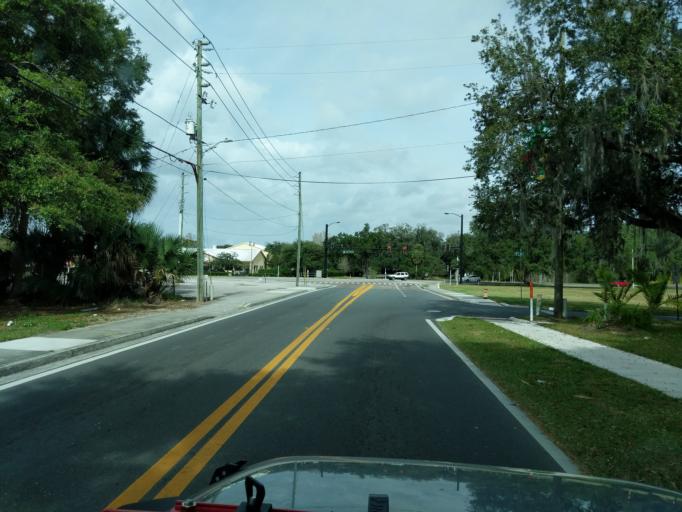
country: US
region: Florida
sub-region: Orange County
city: Winter Garden
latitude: 28.5664
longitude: -81.5754
